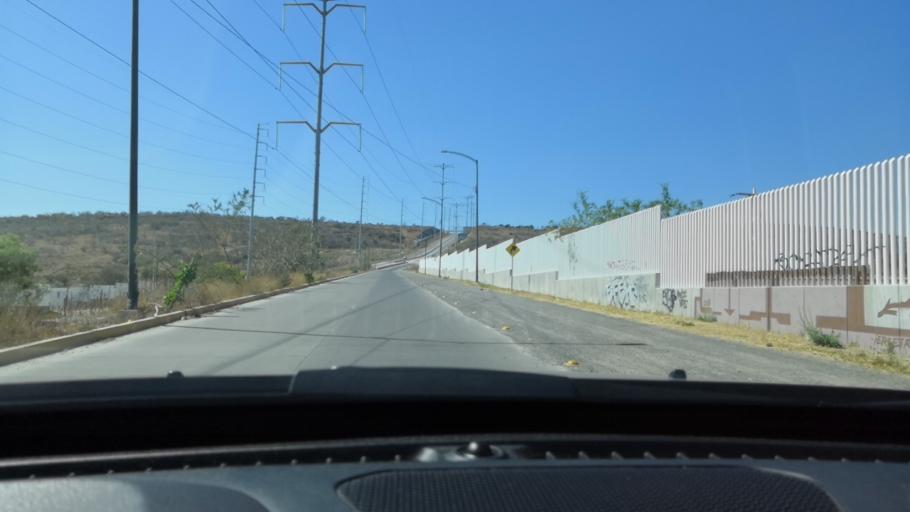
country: MX
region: Guanajuato
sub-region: Leon
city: Centro Familiar la Soledad
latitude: 21.1245
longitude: -101.7383
